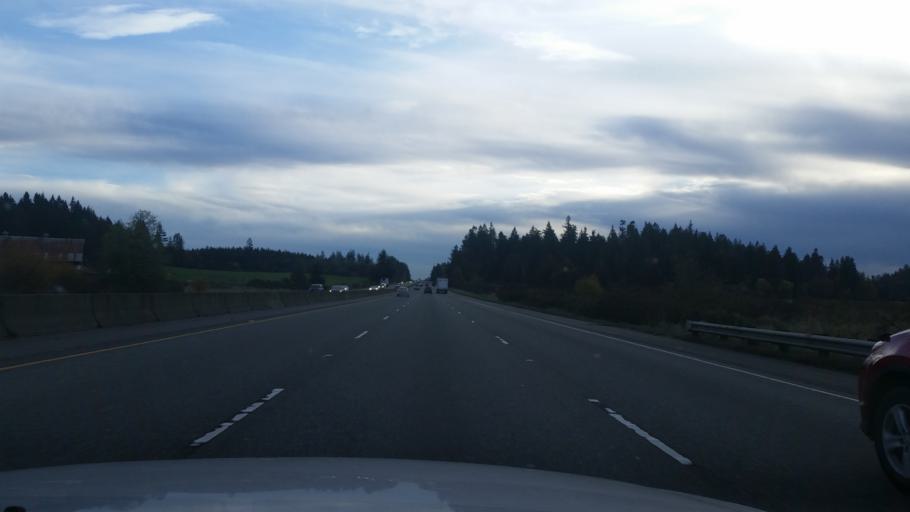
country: US
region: Washington
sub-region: Thurston County
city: Tumwater
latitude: 46.9162
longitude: -122.9499
